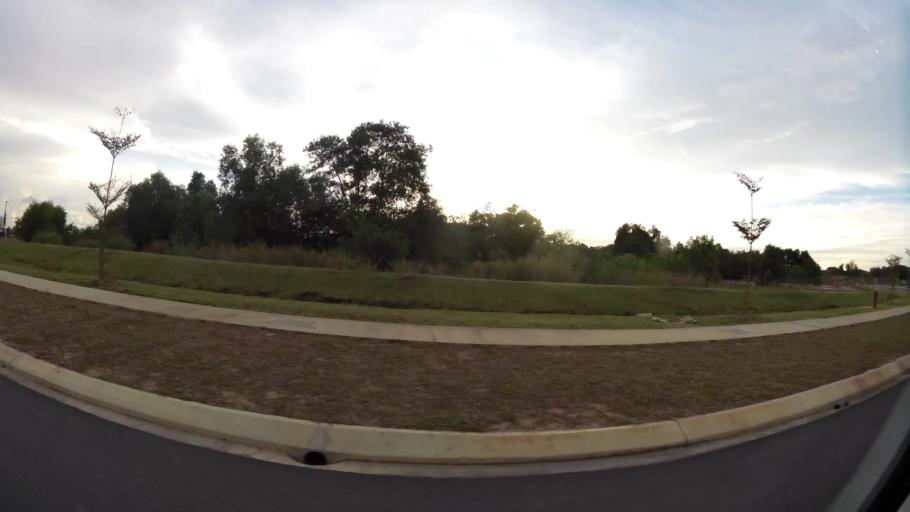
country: BN
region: Brunei and Muara
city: Bandar Seri Begawan
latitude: 4.9930
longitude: 114.9854
